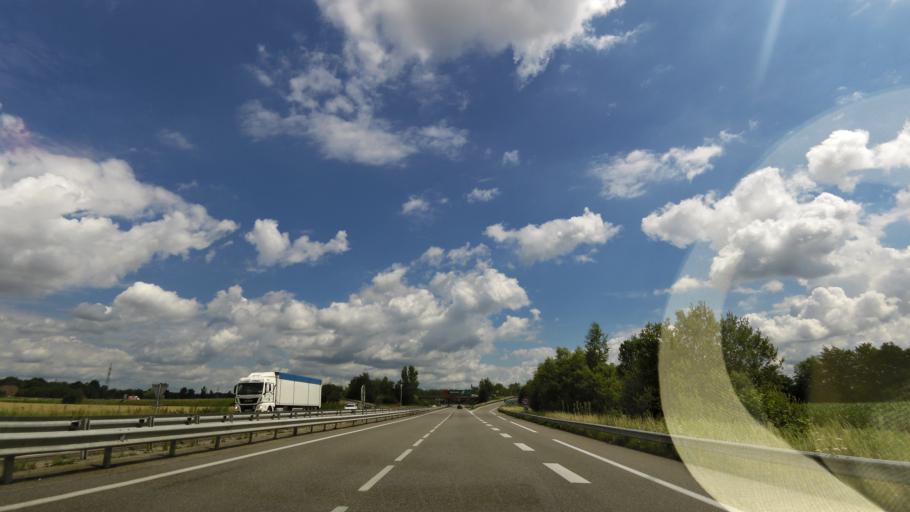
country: FR
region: Alsace
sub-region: Departement du Bas-Rhin
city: Herrlisheim
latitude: 48.7456
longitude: 7.9123
